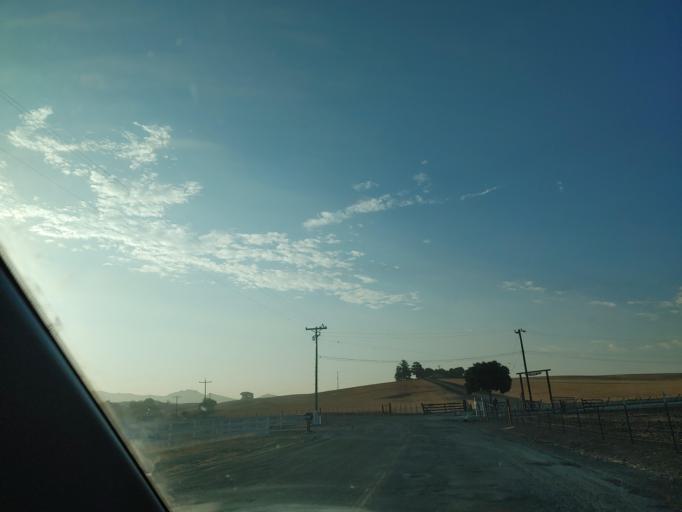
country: US
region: California
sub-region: San Benito County
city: Ridgemark
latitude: 36.8587
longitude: -121.3371
